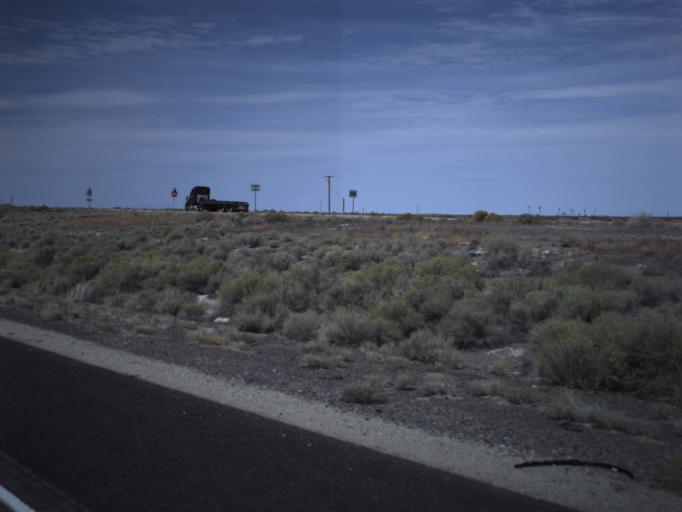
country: US
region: Utah
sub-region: Tooele County
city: Wendover
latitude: 40.7273
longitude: -113.2567
